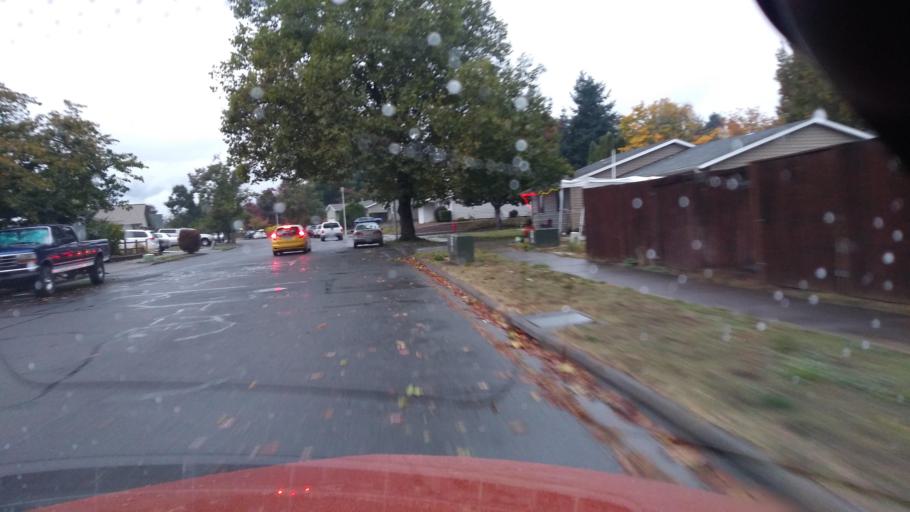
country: US
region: Oregon
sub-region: Washington County
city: Forest Grove
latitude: 45.5276
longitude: -123.1338
